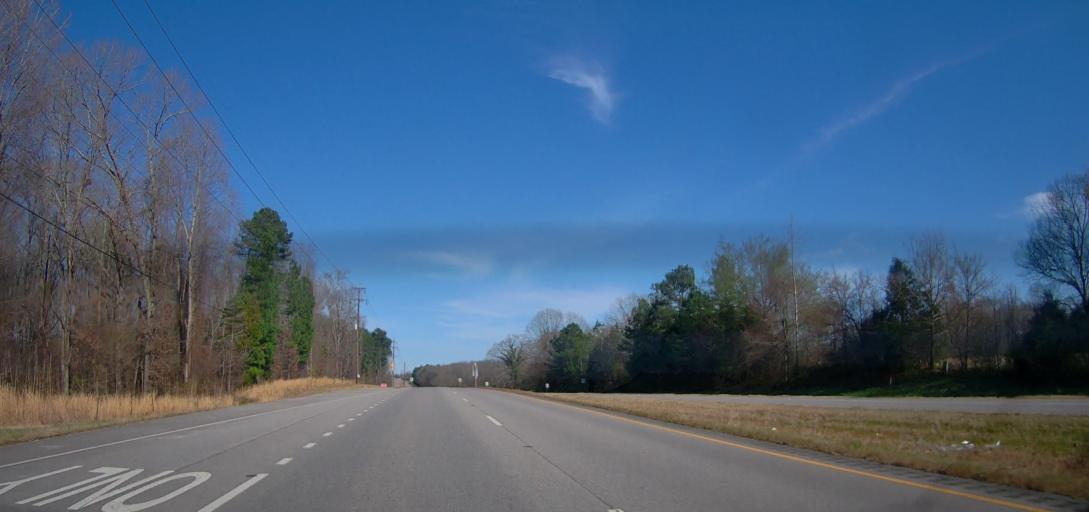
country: US
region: Alabama
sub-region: Lauderdale County
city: Killen
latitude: 34.8598
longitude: -87.4908
